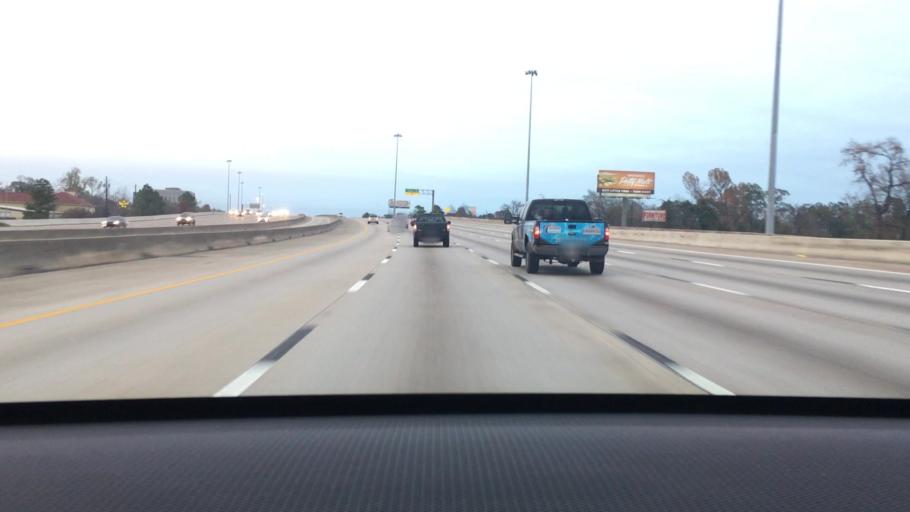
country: US
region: Texas
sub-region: Harris County
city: Houston
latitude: 29.8367
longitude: -95.3335
